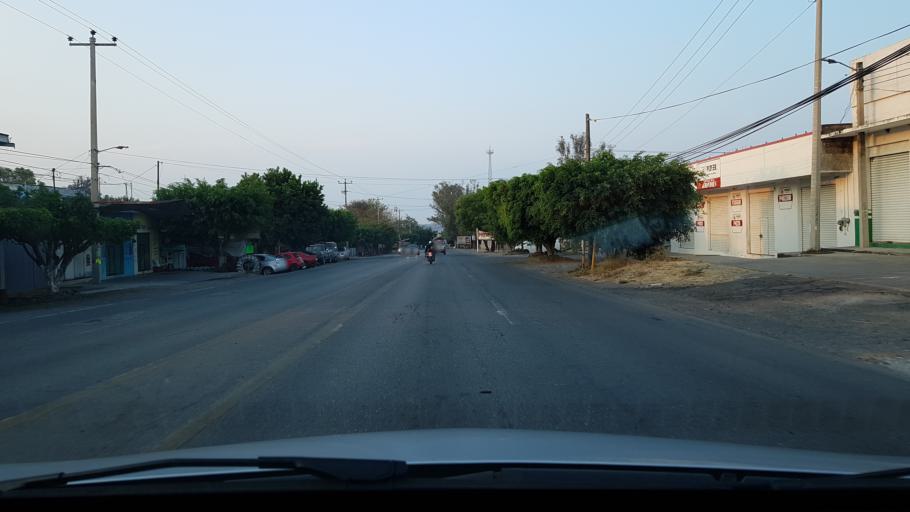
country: MX
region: Morelos
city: Jonacatepec de Leandro Valle
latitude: 18.6903
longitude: -98.8020
